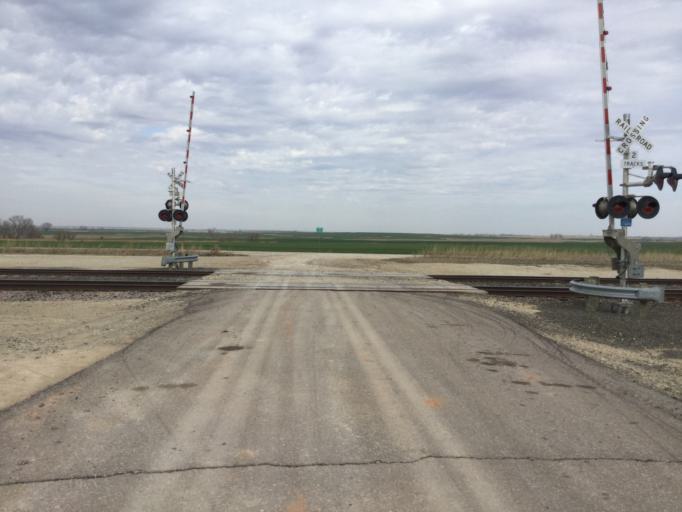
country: US
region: Kansas
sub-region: Barber County
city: Kiowa
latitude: 37.0651
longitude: -98.4399
